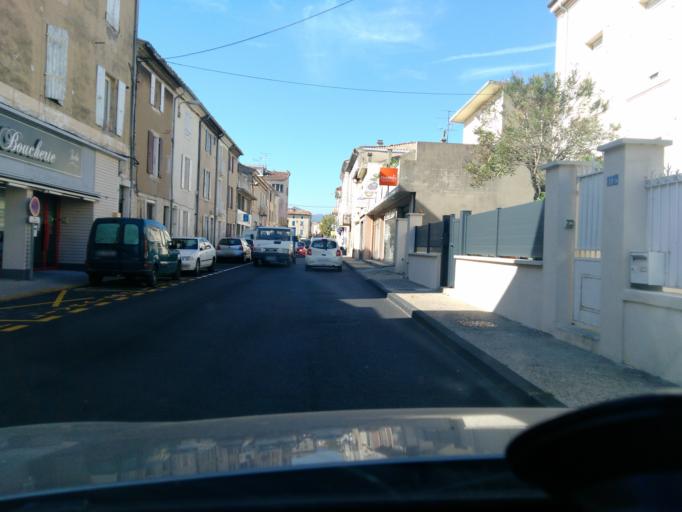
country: FR
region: Rhone-Alpes
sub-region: Departement de la Drome
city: Montelimar
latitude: 44.5563
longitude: 4.7562
